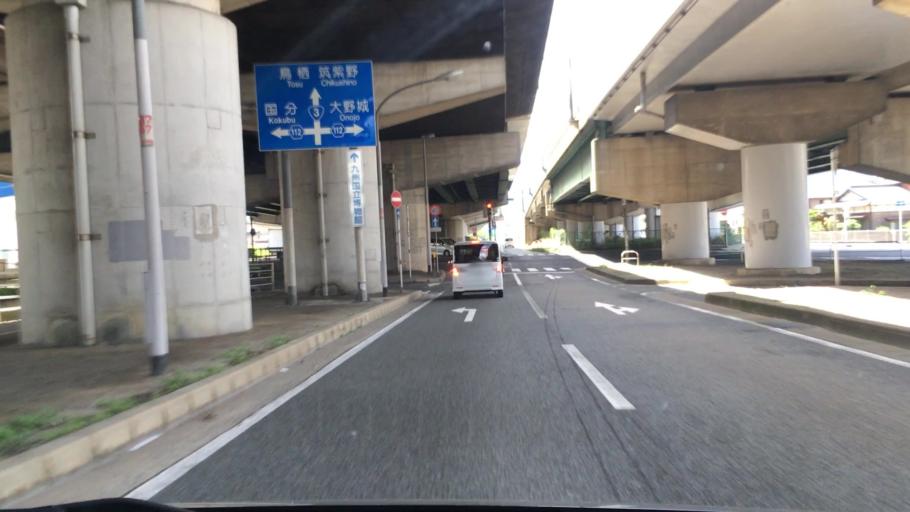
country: JP
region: Fukuoka
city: Onojo
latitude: 33.5252
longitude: 130.4956
